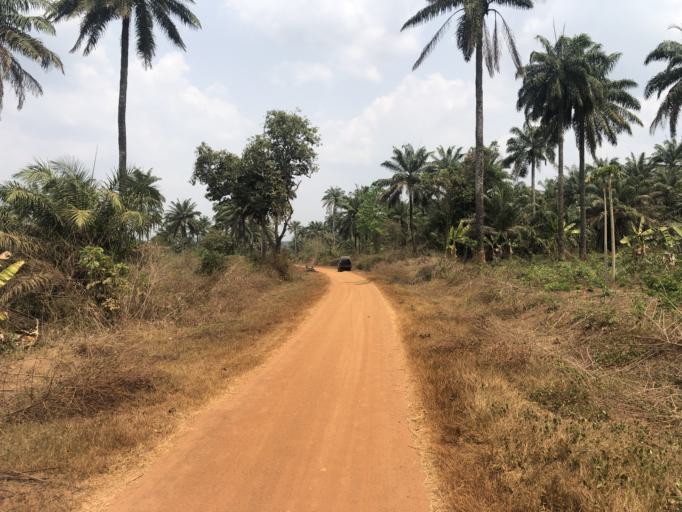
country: NG
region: Osun
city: Bode Osi
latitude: 7.7593
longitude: 4.2689
